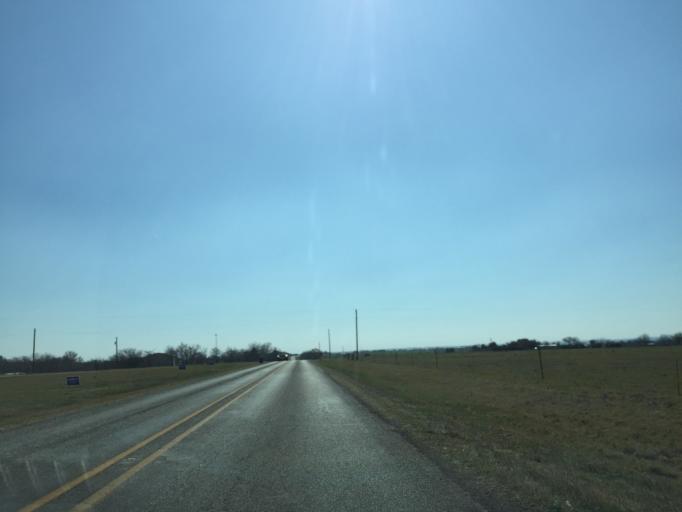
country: US
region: Texas
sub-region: Williamson County
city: Serenada
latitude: 30.6990
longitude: -97.5888
